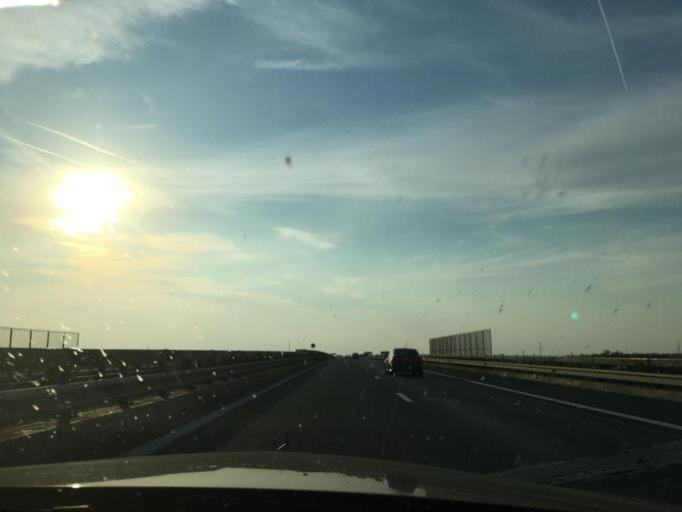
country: RO
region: Ilfov
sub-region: Comuna Cernica
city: Caldararu
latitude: 44.4087
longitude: 26.2617
